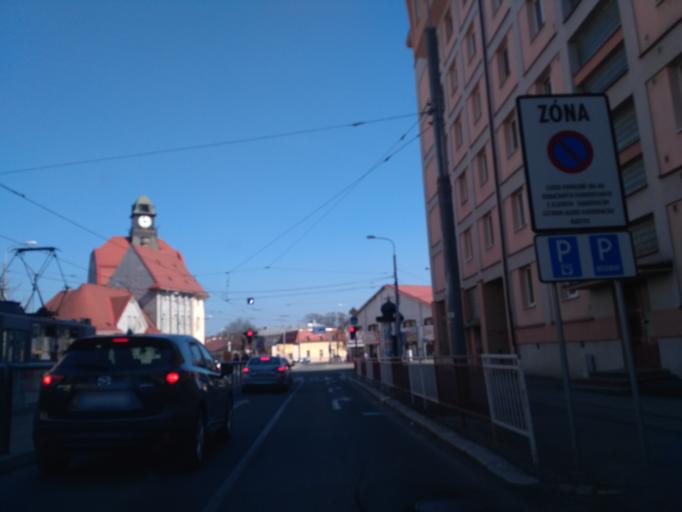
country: SK
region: Kosicky
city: Kosice
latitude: 48.7265
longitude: 21.2489
